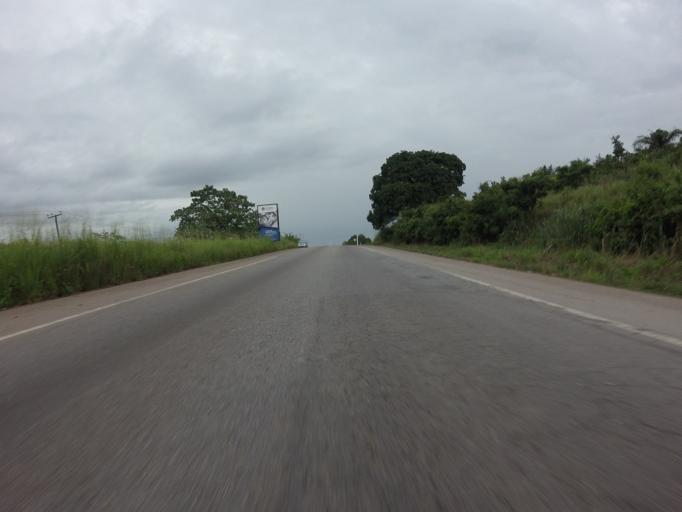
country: GH
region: Ashanti
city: Konongo
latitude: 6.6111
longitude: -1.2423
